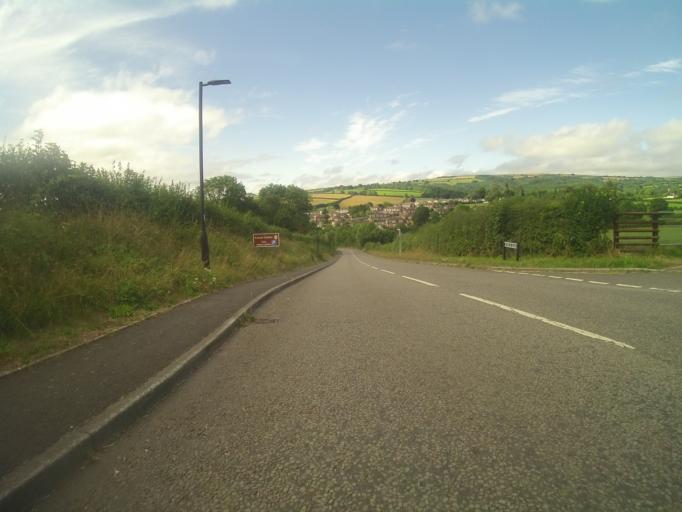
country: GB
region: England
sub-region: Devon
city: Buckfastleigh
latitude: 50.4878
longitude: -3.7817
